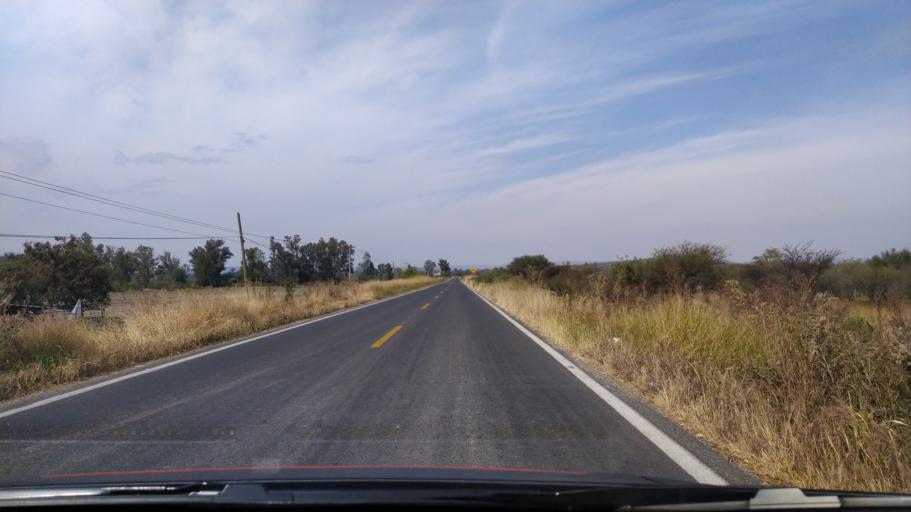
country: MX
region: Guanajuato
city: Ciudad Manuel Doblado
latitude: 20.7796
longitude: -101.9780
